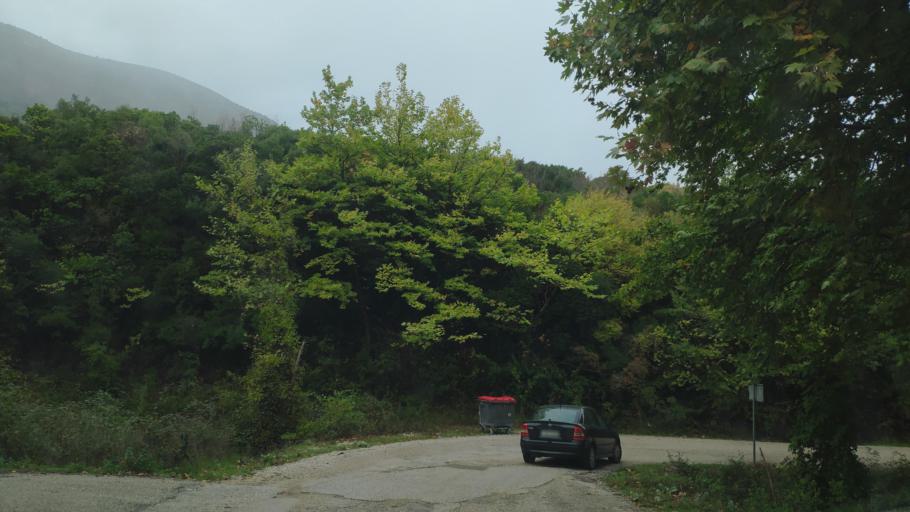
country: GR
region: Epirus
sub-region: Nomos Thesprotias
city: Paramythia
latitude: 39.4721
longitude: 20.6687
